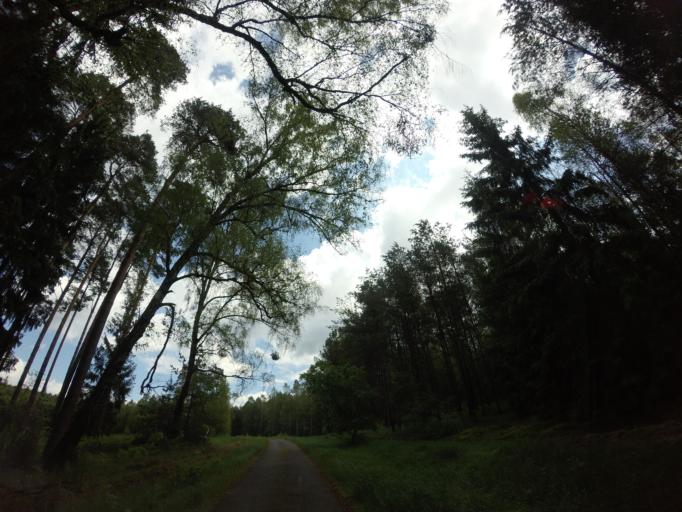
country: PL
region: West Pomeranian Voivodeship
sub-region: Powiat drawski
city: Kalisz Pomorski
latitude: 53.2250
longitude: 15.9102
